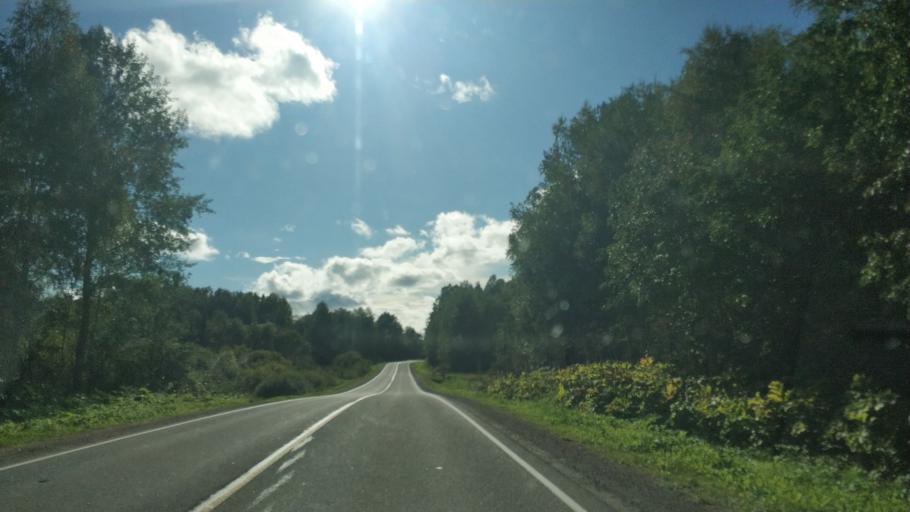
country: RU
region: Republic of Karelia
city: Khelyulya
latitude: 61.6512
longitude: 30.6034
